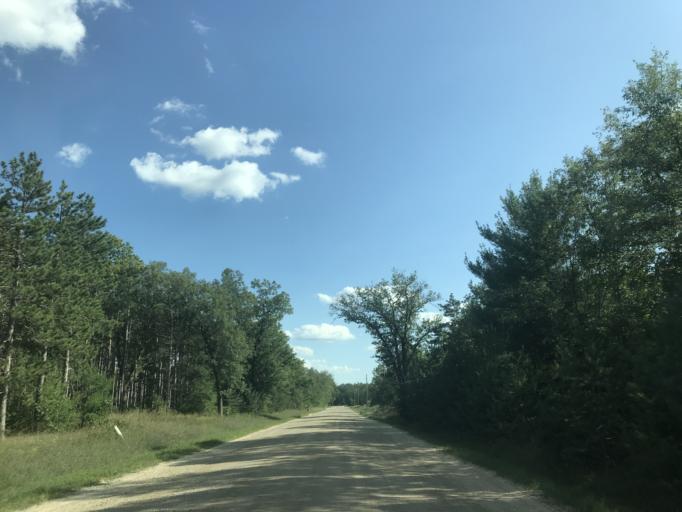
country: US
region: Michigan
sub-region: Newaygo County
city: Newaygo
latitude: 43.4404
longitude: -85.7326
